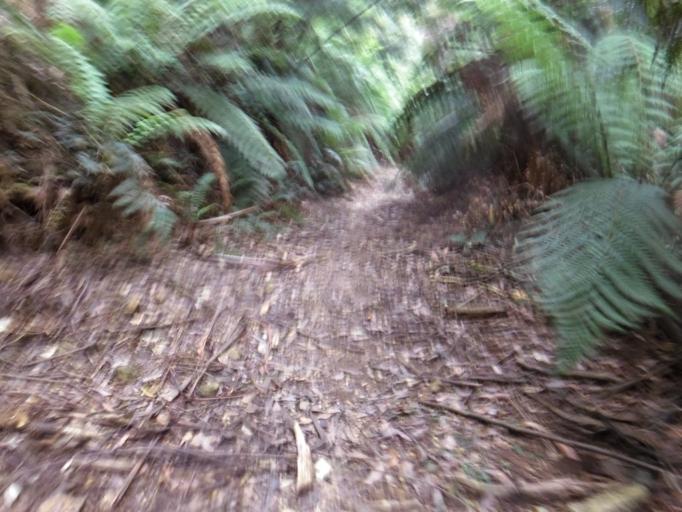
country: AU
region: Victoria
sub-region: Yarra Ranges
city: Healesville
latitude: -37.5100
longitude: 145.5200
